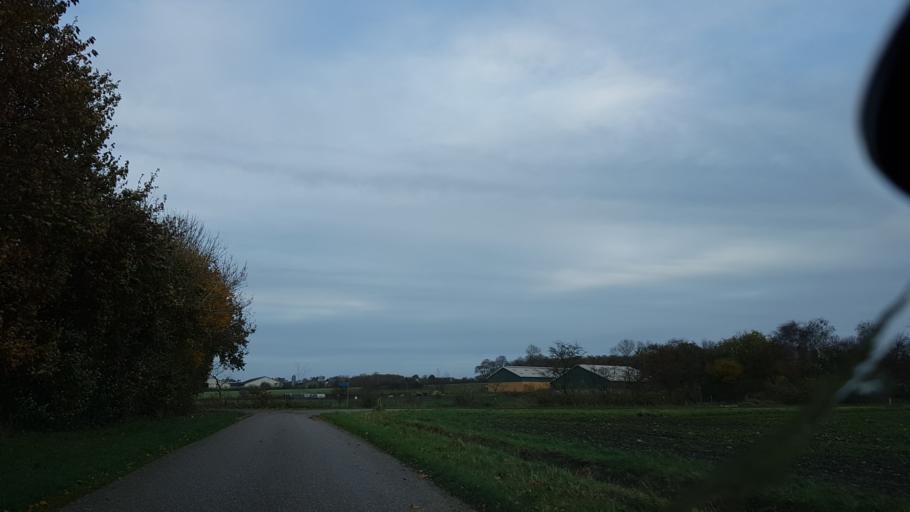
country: DK
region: South Denmark
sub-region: Haderslev Kommune
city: Vojens
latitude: 55.2506
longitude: 9.1861
